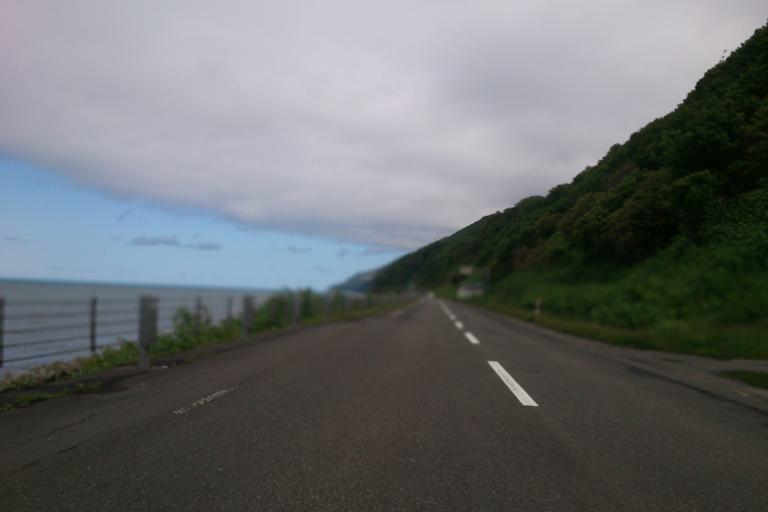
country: JP
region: Hokkaido
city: Ishikari
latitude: 43.4293
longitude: 141.4213
